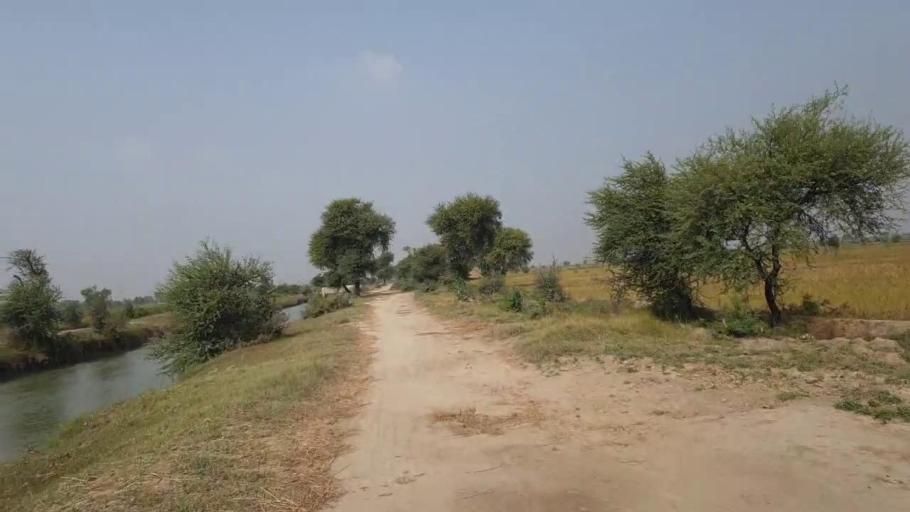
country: PK
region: Sindh
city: Kario
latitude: 24.8393
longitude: 68.5401
